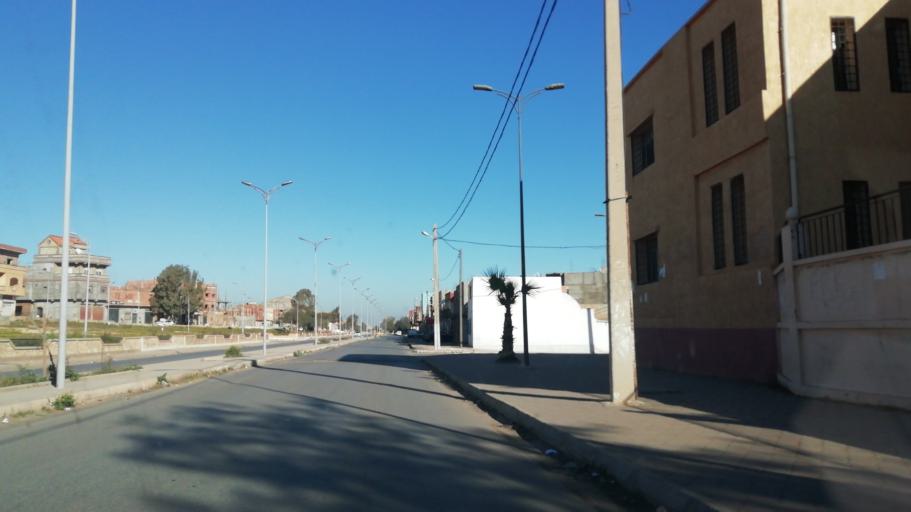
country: DZ
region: Oran
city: Bir el Djir
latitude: 35.7192
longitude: -0.5486
